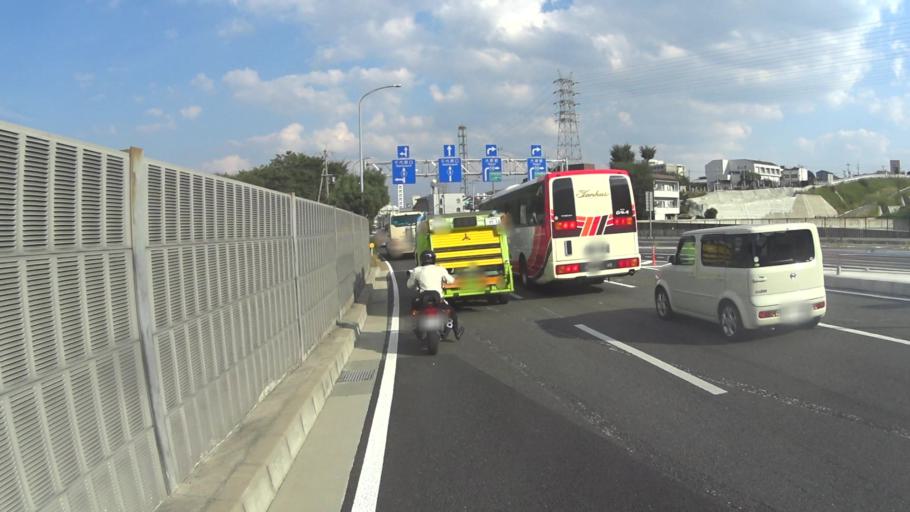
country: JP
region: Kyoto
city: Muko
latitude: 34.9768
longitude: 135.6600
